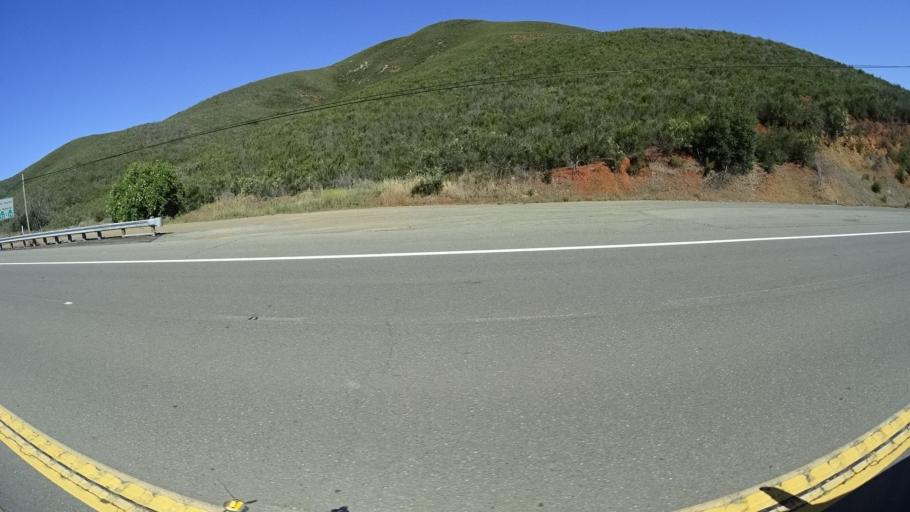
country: US
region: California
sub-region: Lake County
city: Clearlake
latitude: 39.0137
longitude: -122.6032
